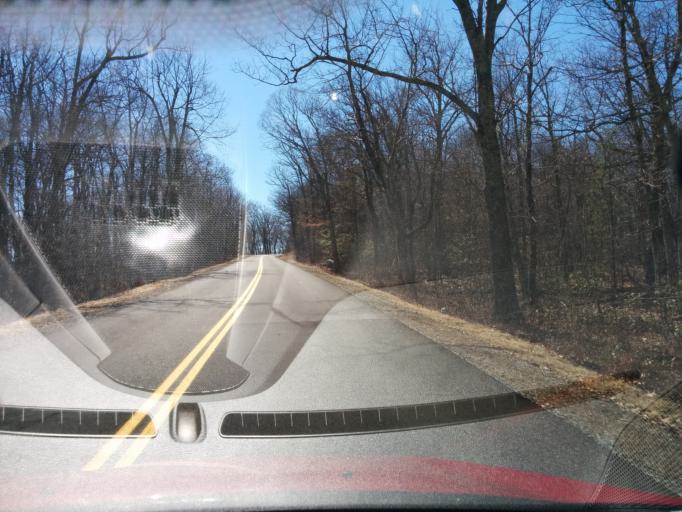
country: US
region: Virginia
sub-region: Augusta County
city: Stuarts Draft
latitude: 37.9135
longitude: -79.0811
